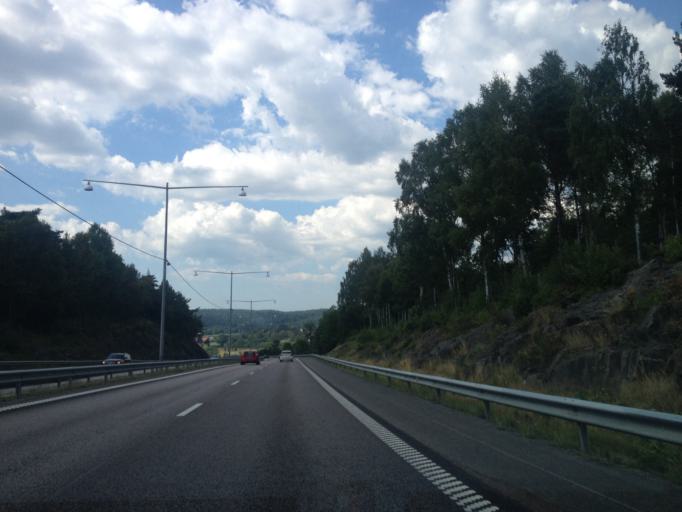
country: SE
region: Vaestra Goetaland
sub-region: Partille Kommun
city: Furulund
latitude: 57.7417
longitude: 12.1683
